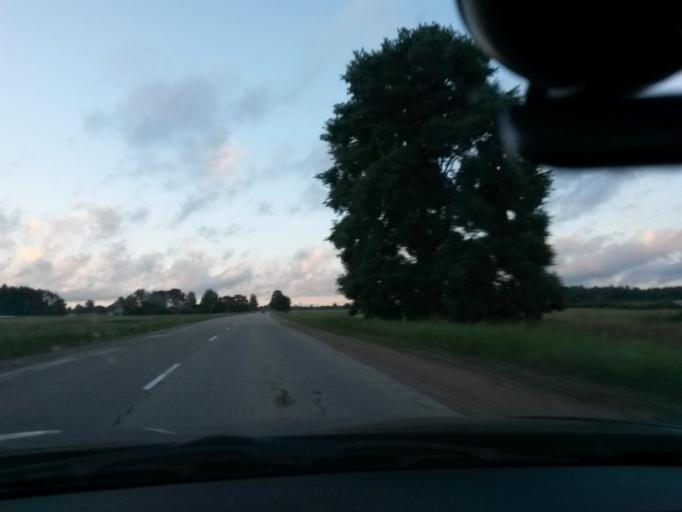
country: LV
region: Jekabpils Rajons
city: Jekabpils
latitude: 56.7085
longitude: 25.9832
